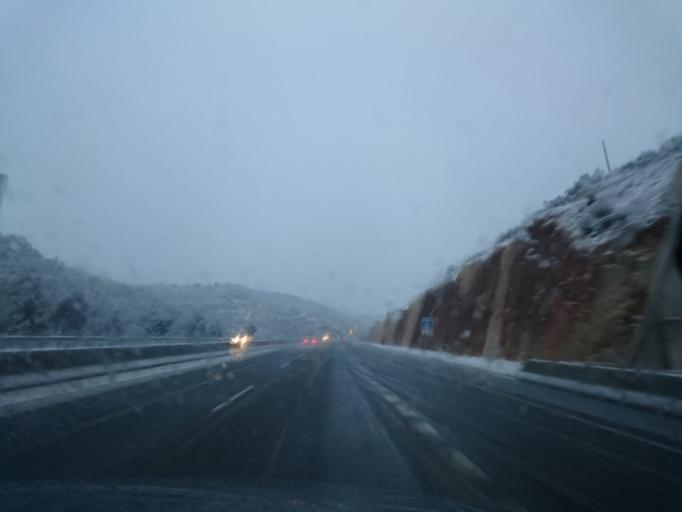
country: ES
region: Catalonia
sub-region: Provincia de Barcelona
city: Sant Pere de Ribes
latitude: 41.2937
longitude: 1.7257
